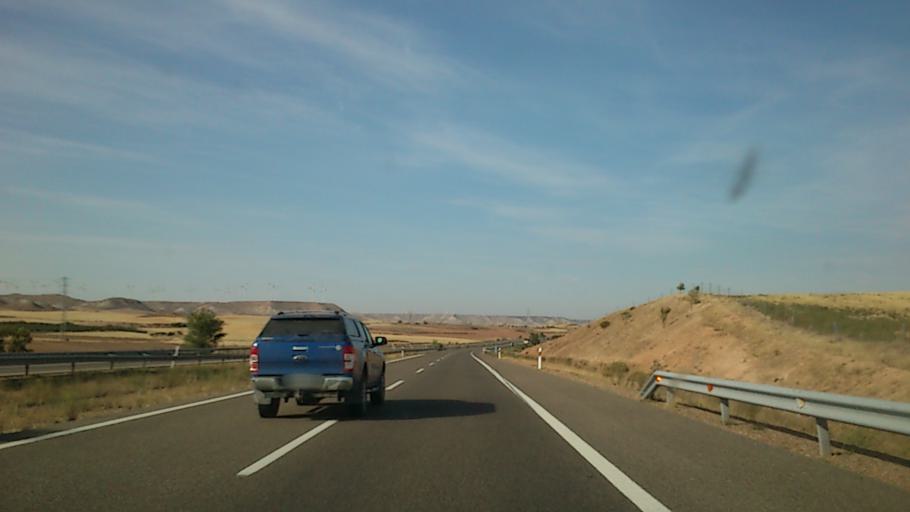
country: ES
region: Aragon
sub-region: Provincia de Zaragoza
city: Longares
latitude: 41.4372
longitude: -1.1432
